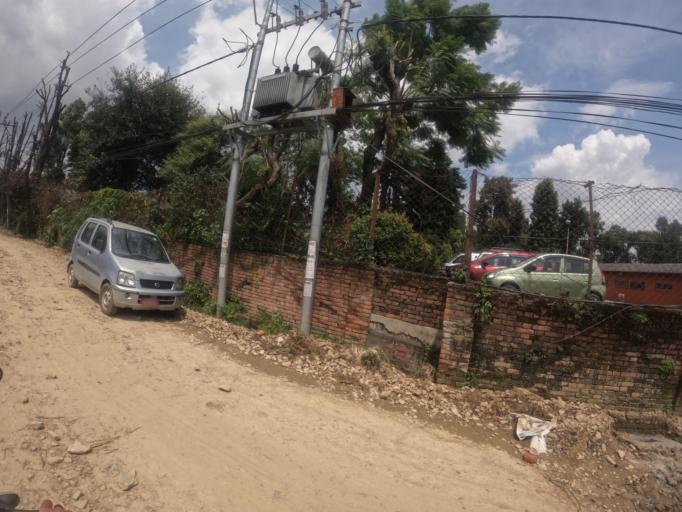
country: NP
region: Central Region
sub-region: Bagmati Zone
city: Bhaktapur
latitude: 27.6805
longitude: 85.3750
